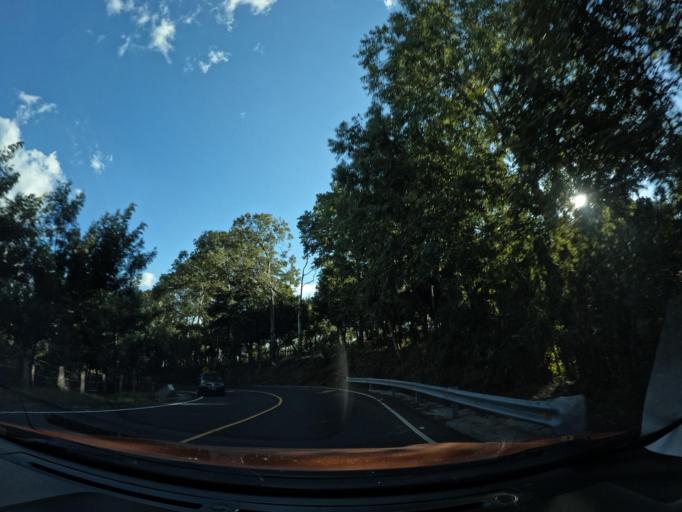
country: GT
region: Escuintla
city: Palin
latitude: 14.4564
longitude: -90.6947
